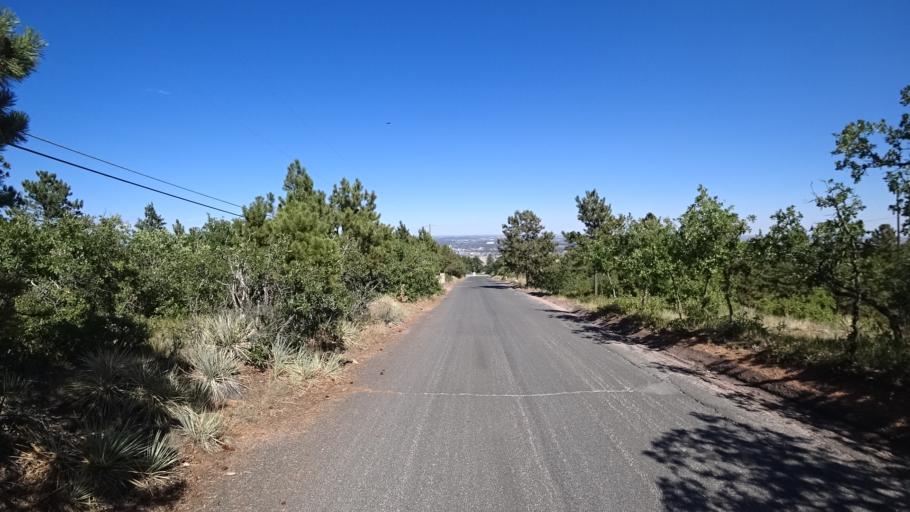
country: US
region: Colorado
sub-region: El Paso County
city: Colorado Springs
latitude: 38.8133
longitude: -104.8747
